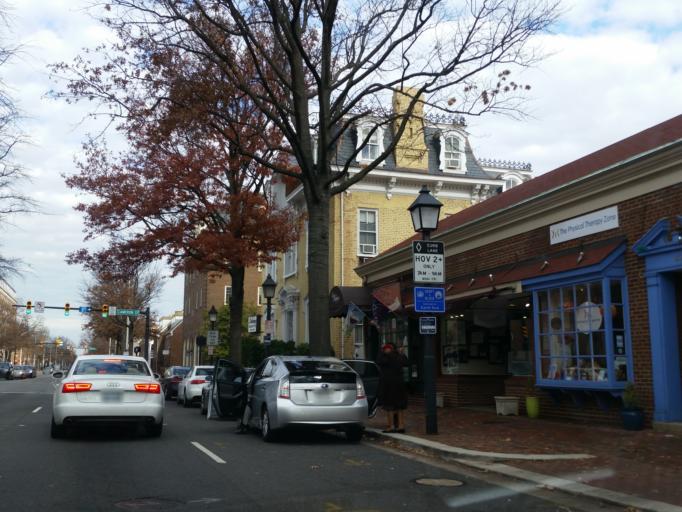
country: US
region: Virginia
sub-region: City of Alexandria
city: Alexandria
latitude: 38.8057
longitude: -77.0468
